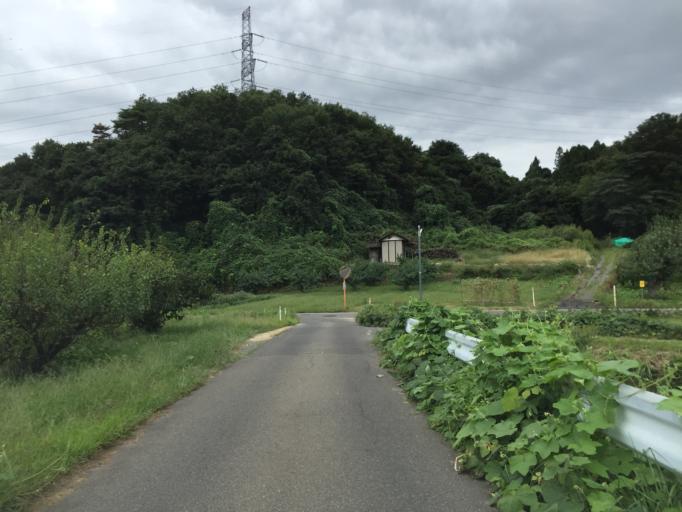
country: JP
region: Fukushima
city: Hobaramachi
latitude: 37.8007
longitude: 140.5098
